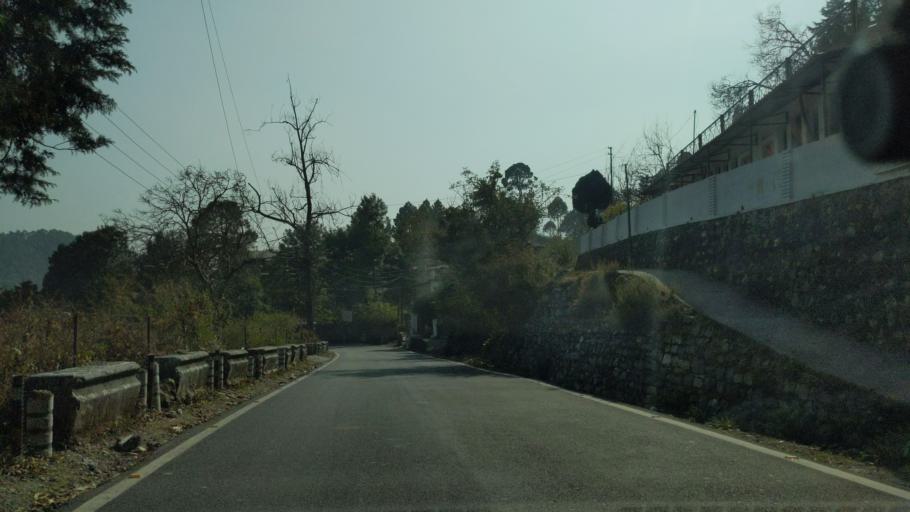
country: IN
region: Uttarakhand
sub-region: Naini Tal
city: Bhowali
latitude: 29.3787
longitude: 79.5178
